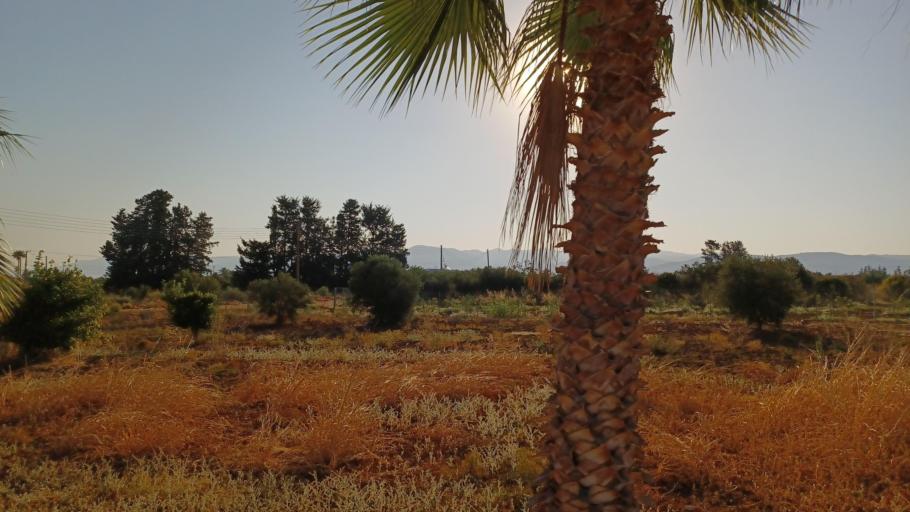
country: CY
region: Pafos
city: Polis
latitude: 35.0324
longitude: 32.3900
